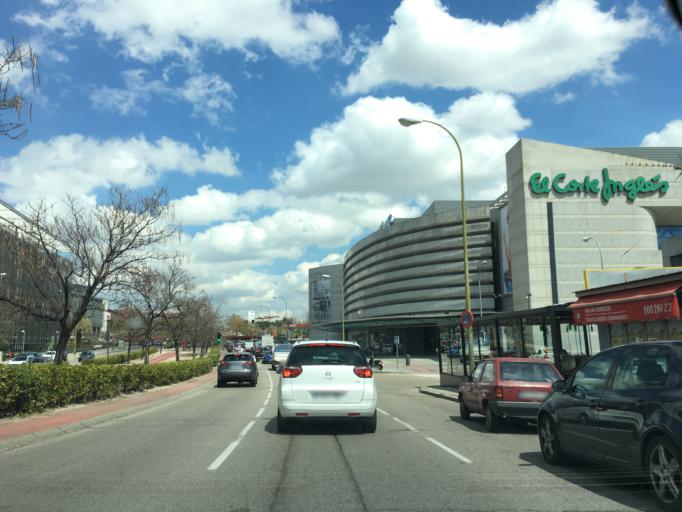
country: ES
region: Madrid
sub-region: Provincia de Madrid
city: San Blas
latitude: 40.4560
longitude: -3.6191
